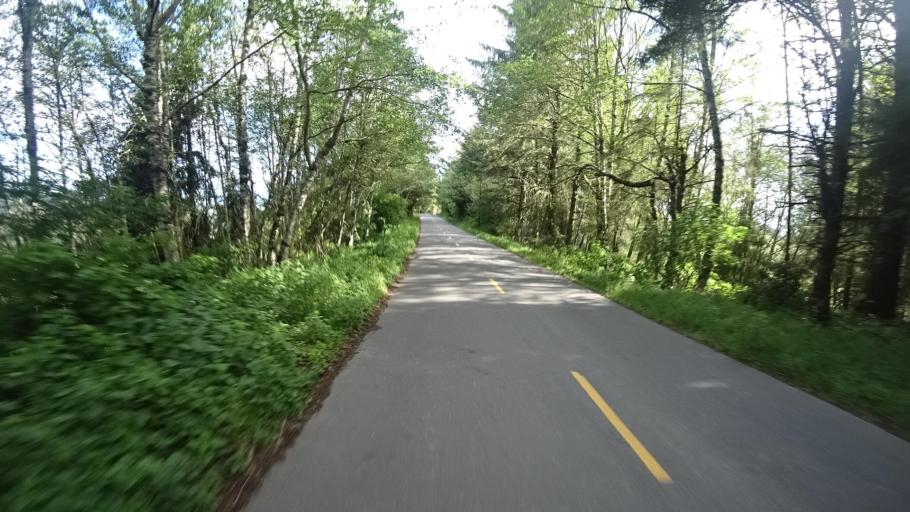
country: US
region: California
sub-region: Humboldt County
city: Ferndale
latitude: 40.5577
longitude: -124.2730
